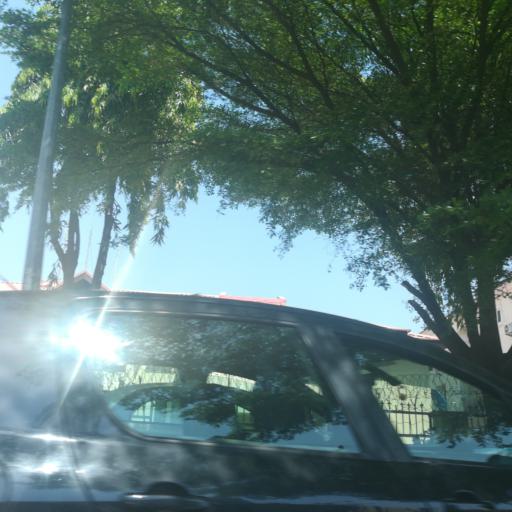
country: NG
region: Abuja Federal Capital Territory
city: Abuja
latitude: 9.0742
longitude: 7.4494
